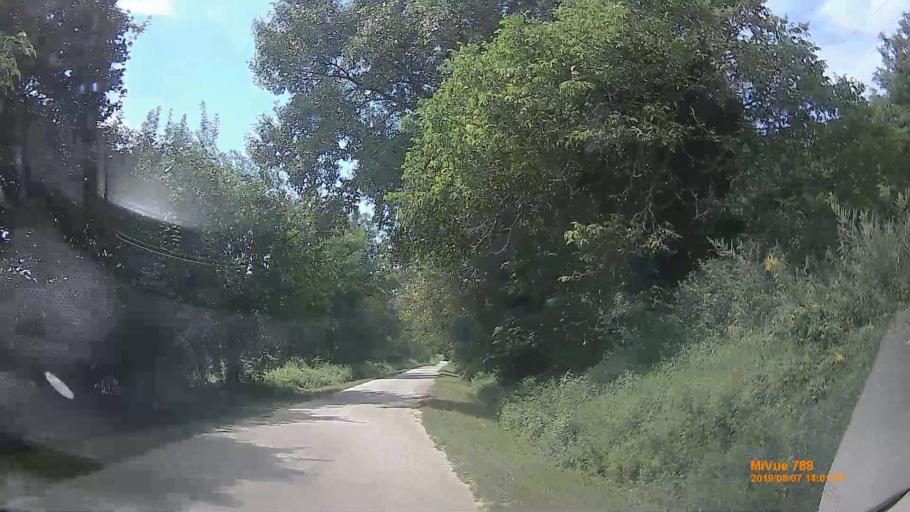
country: HU
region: Zala
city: Zalaszentgrot
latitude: 46.8984
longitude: 17.1661
